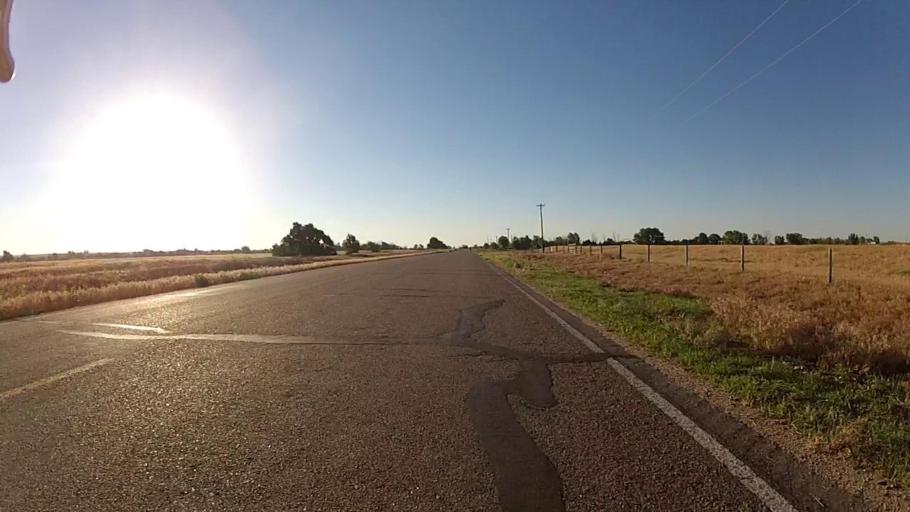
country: US
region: Kansas
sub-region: Ford County
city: Dodge City
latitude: 37.7098
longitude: -99.9157
